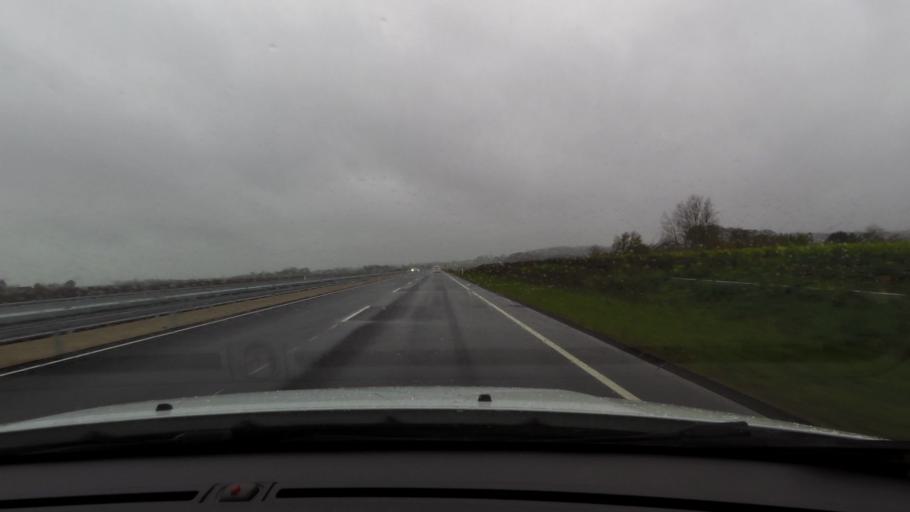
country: DK
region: Capital Region
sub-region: Frederikssund Kommune
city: Skibby
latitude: 55.7949
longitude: 11.9844
